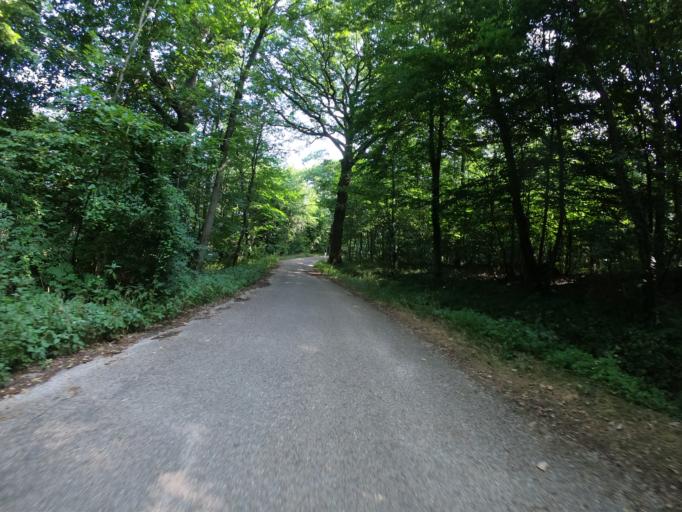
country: FR
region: Ile-de-France
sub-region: Departement de l'Essonne
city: Bievres
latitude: 48.7619
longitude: 2.2338
